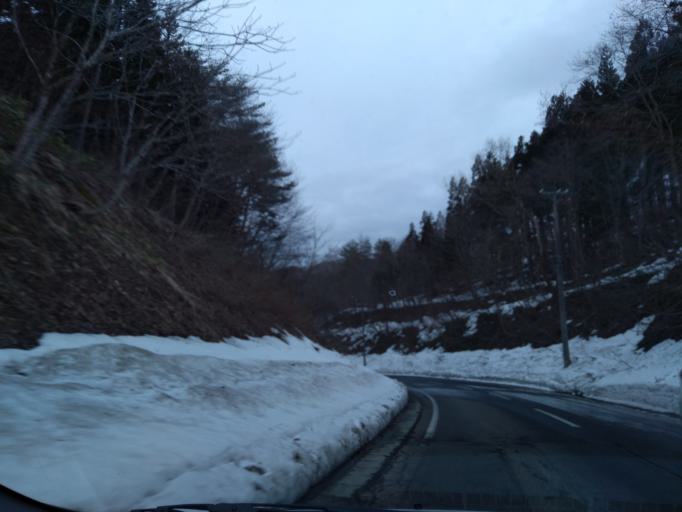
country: JP
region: Iwate
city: Kitakami
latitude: 39.2376
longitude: 140.9551
